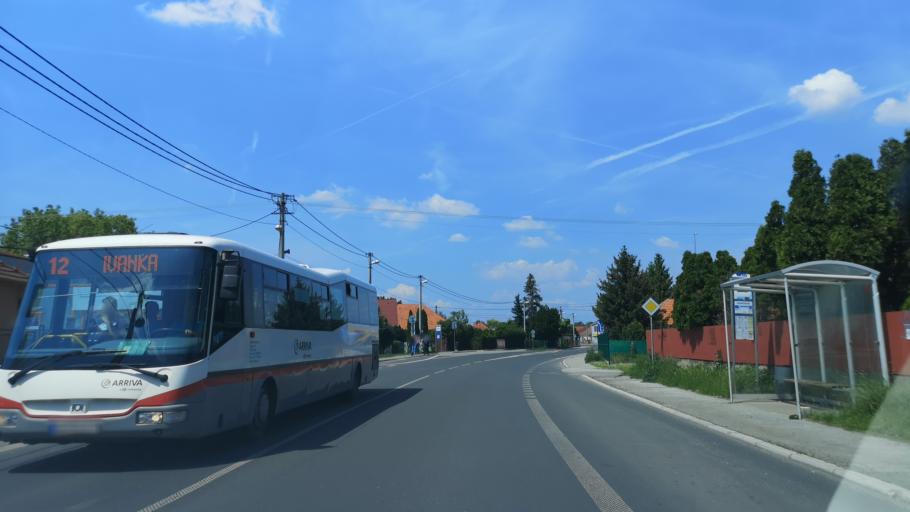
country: SK
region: Nitriansky
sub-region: Okres Nitra
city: Nitra
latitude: 48.2689
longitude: 18.1014
